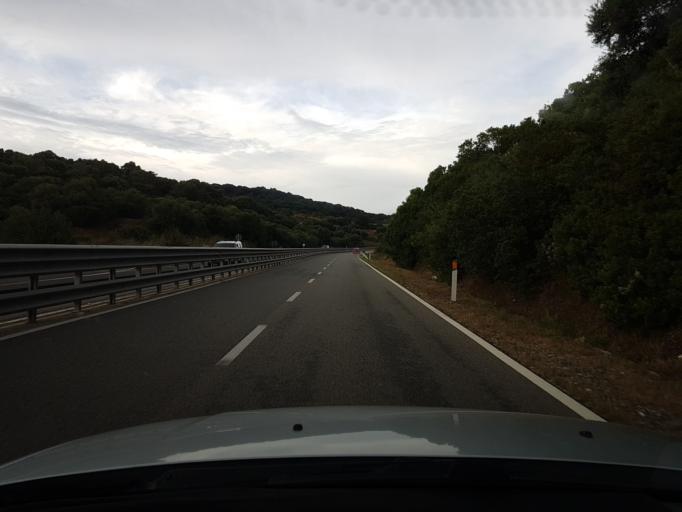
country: IT
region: Sardinia
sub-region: Provincia di Oristano
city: Sedilo
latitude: 40.1560
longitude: 8.9054
